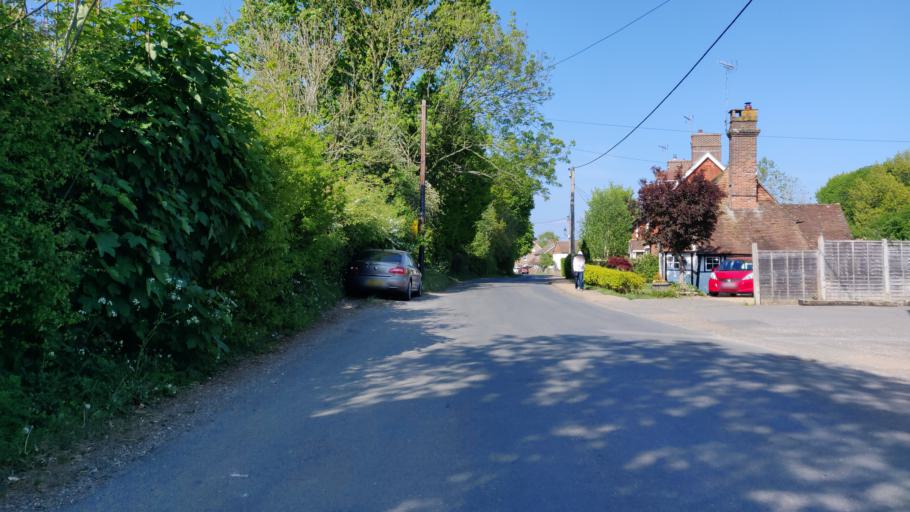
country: GB
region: England
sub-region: West Sussex
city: Southwater
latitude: 51.0317
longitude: -0.3955
